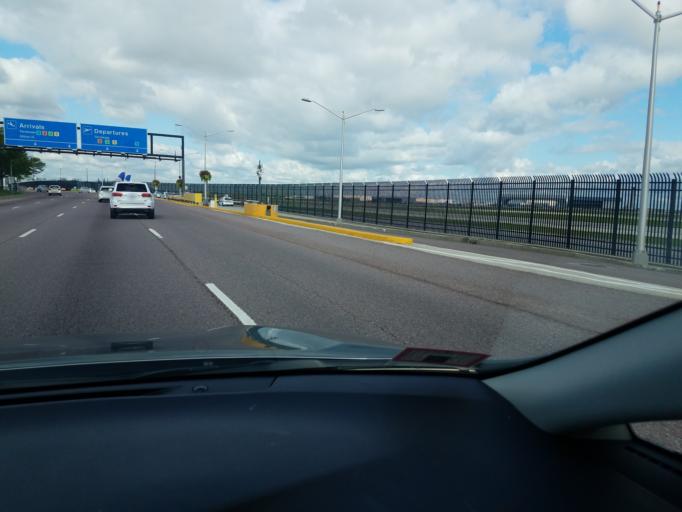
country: US
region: Illinois
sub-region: Cook County
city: Rosemont
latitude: 41.9821
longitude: -87.9005
